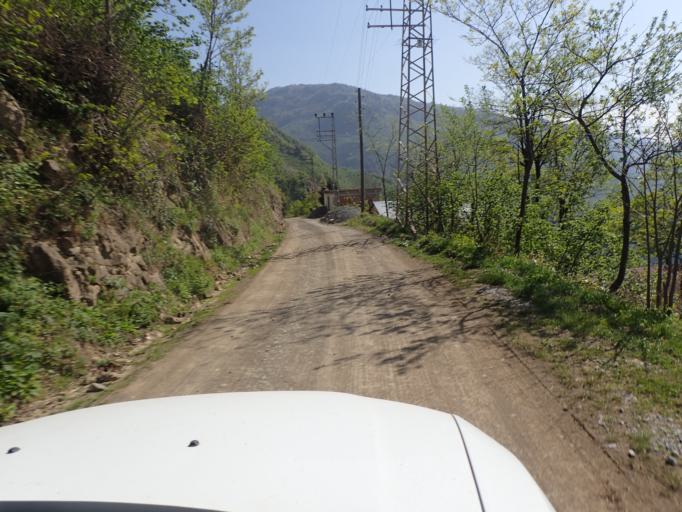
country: TR
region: Ordu
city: Kabaduz
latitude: 40.7274
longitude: 37.8707
